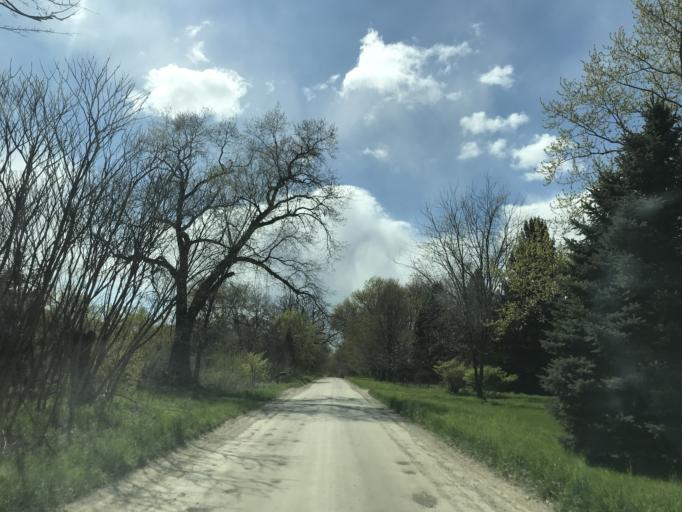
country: US
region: Michigan
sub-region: Oakland County
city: South Lyon
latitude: 42.4037
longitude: -83.6795
